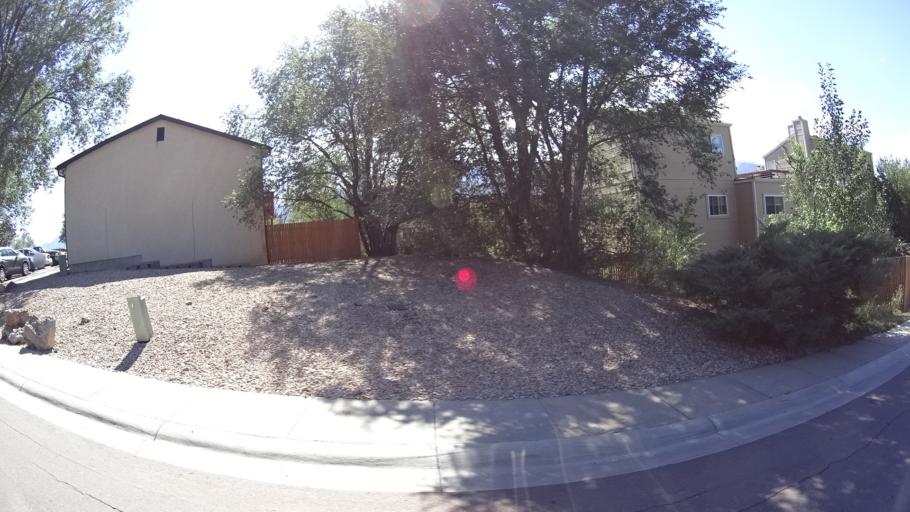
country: US
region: Colorado
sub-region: El Paso County
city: Colorado Springs
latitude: 38.8564
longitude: -104.8626
